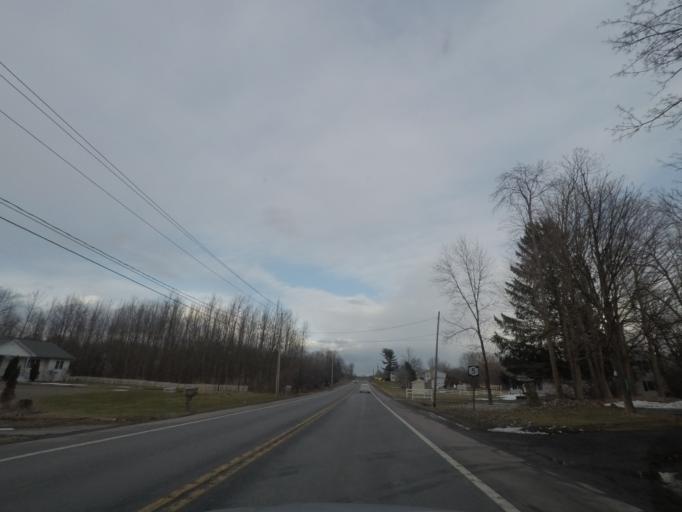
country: US
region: New York
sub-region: Oneida County
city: Vernon
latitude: 43.0744
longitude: -75.4661
